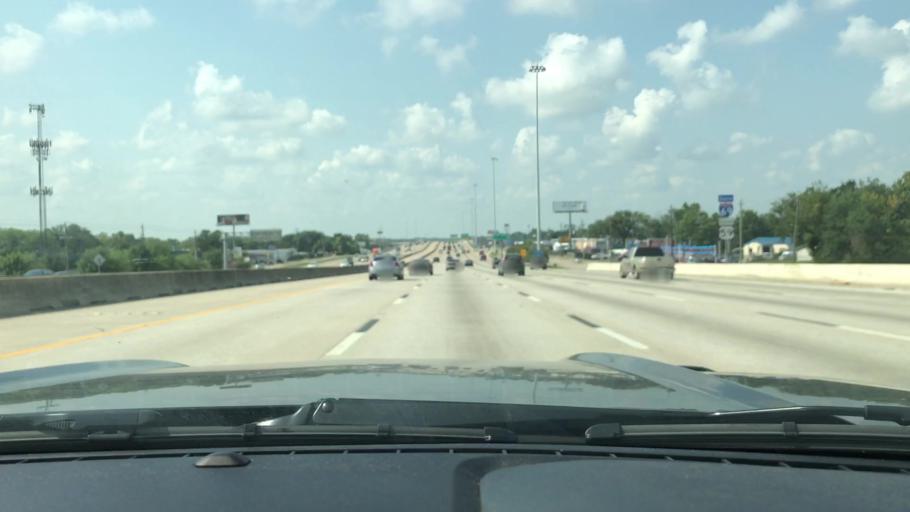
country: US
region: Texas
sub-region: Harris County
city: Aldine
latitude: 29.8782
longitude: -95.3256
